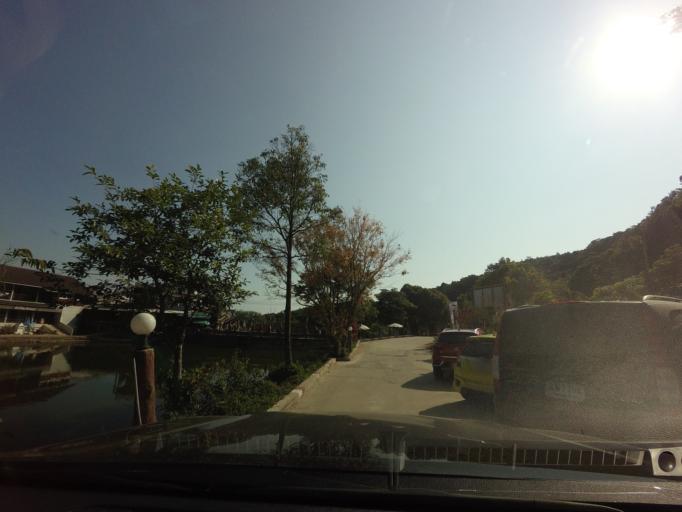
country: TH
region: Kanchanaburi
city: Thong Pha Phum
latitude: 14.6783
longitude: 98.3693
